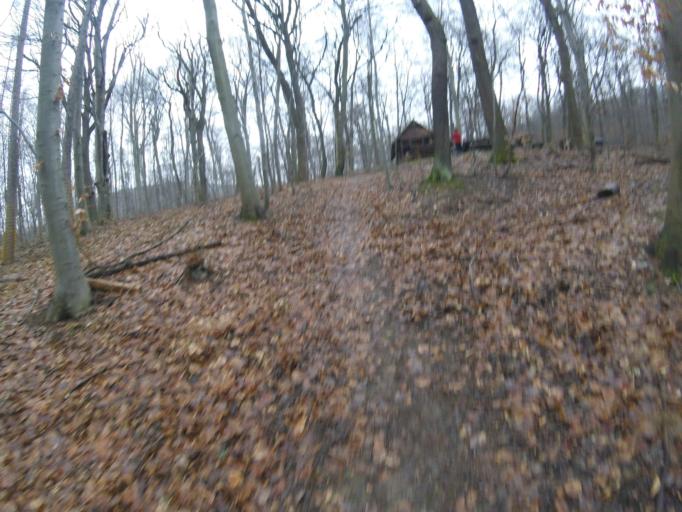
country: HU
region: Pest
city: Visegrad
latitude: 47.7657
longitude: 18.9900
